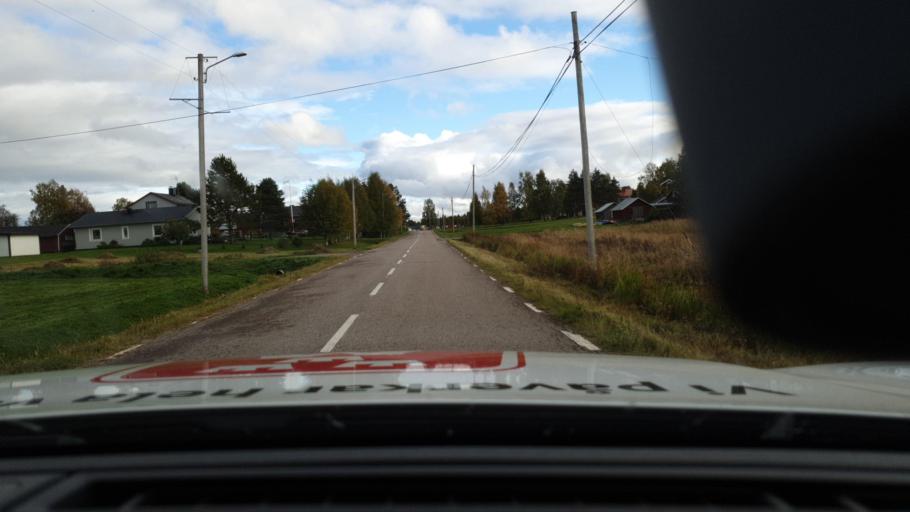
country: SE
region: Norrbotten
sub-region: Overkalix Kommun
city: OEverkalix
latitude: 67.0056
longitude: 22.4900
